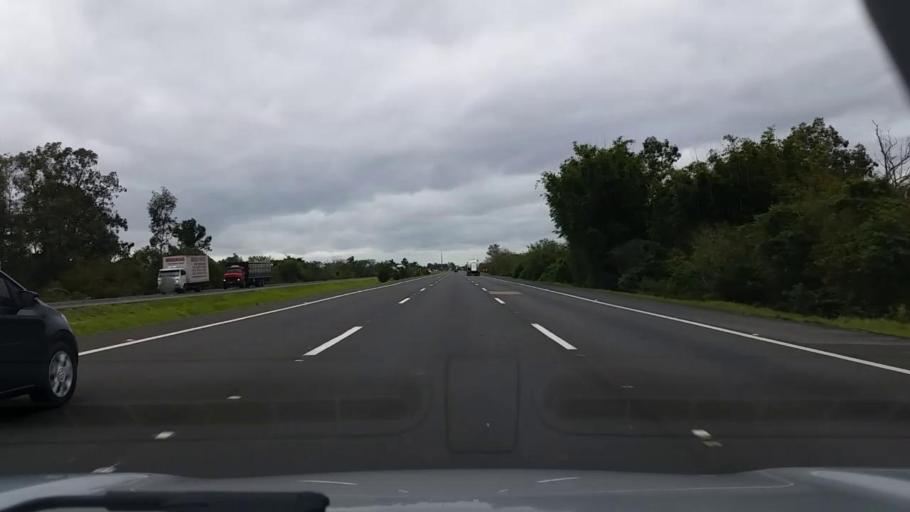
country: BR
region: Rio Grande do Sul
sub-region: Rolante
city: Rolante
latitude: -29.8836
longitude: -50.5560
